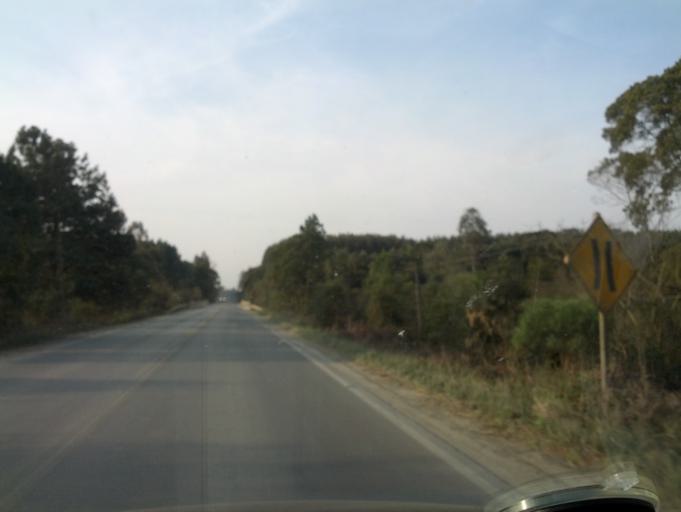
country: BR
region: Santa Catarina
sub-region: Otacilio Costa
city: Otacilio Costa
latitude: -27.5168
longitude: -50.1331
